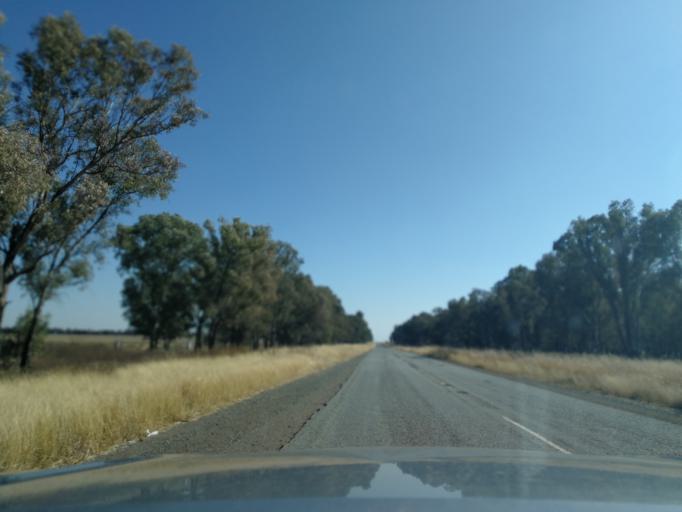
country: ZA
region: Orange Free State
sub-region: Fezile Dabi District Municipality
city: Viljoenskroon
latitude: -27.4024
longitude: 27.0676
